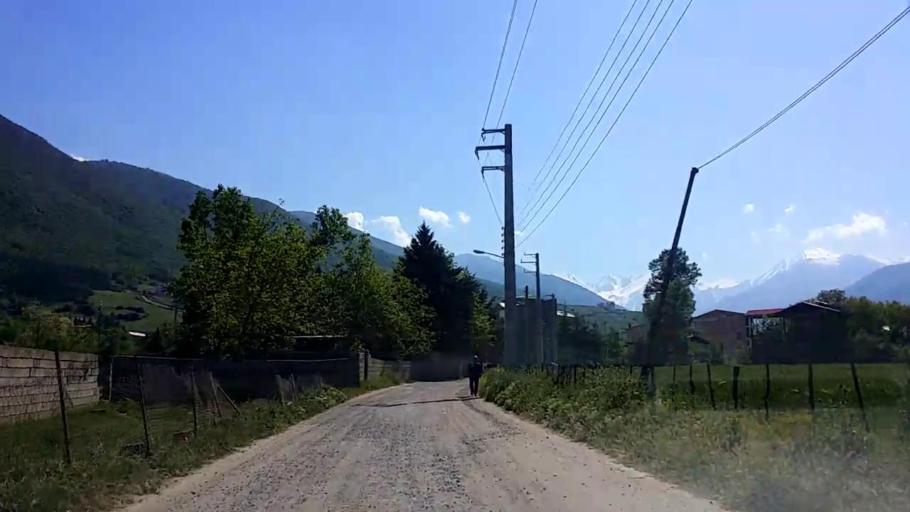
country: IR
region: Mazandaran
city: `Abbasabad
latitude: 36.5093
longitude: 51.1953
